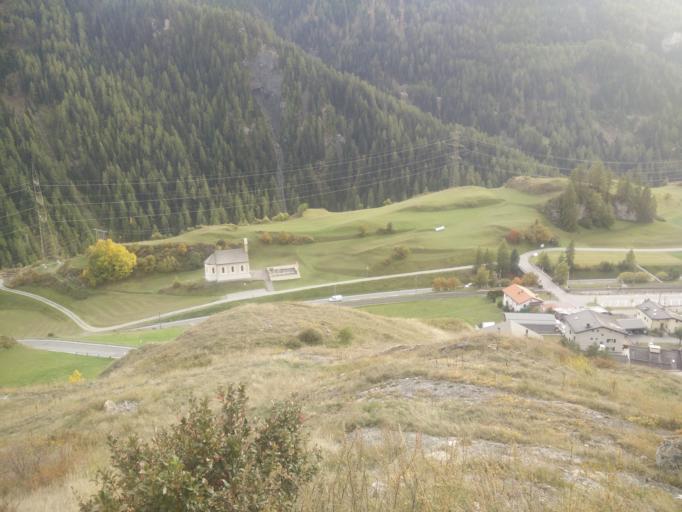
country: CH
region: Grisons
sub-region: Inn District
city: Scuol
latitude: 46.7744
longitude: 10.2045
